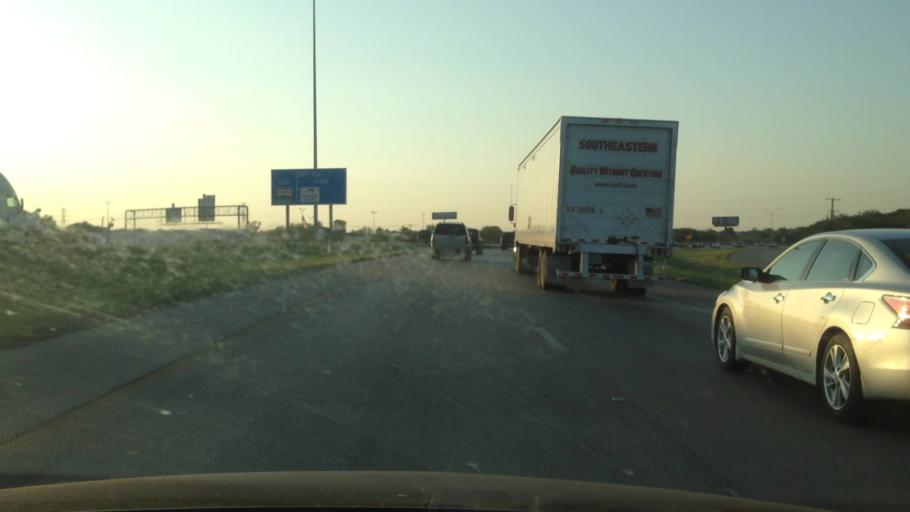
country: US
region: Texas
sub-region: Tarrant County
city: Kennedale
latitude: 32.6711
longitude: -97.2389
